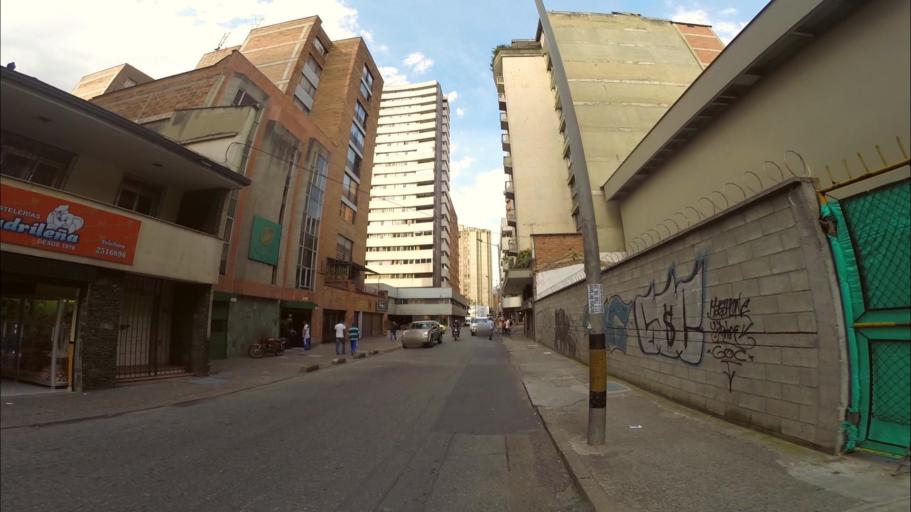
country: CO
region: Antioquia
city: Medellin
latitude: 6.2528
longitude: -75.5636
